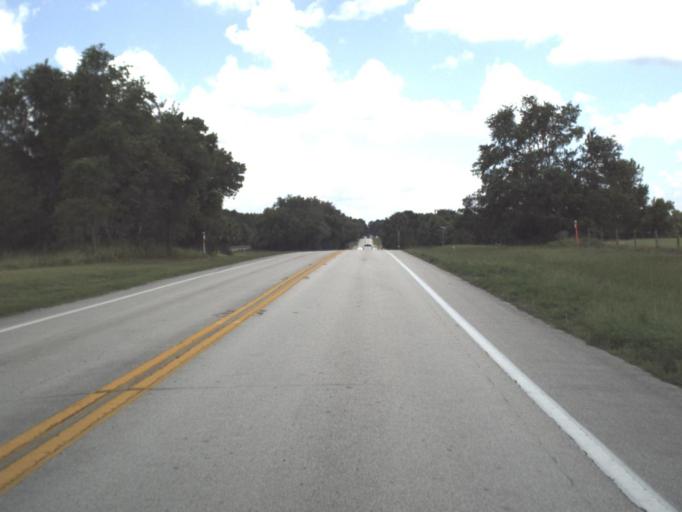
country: US
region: Florida
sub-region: Putnam County
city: Palatka
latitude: 29.5380
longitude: -81.6463
